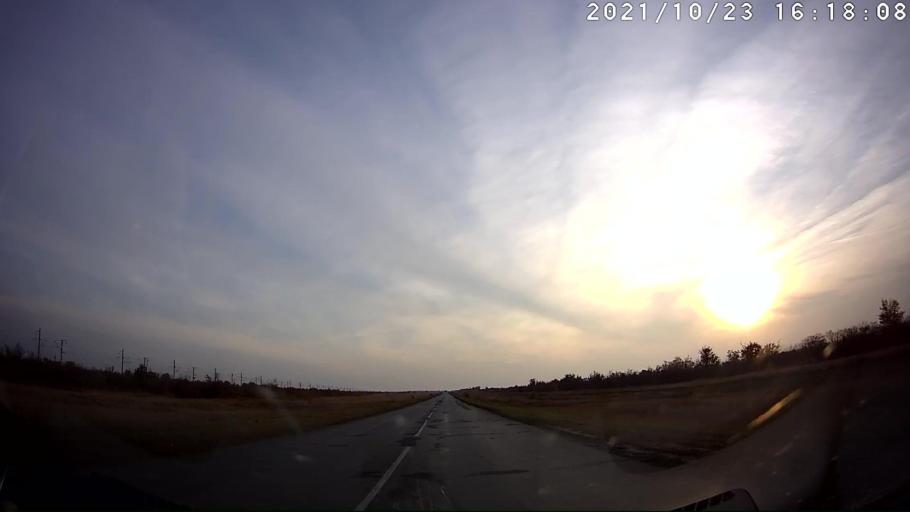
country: RU
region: Volgograd
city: Kotel'nikovo
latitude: 47.9045
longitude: 43.5511
